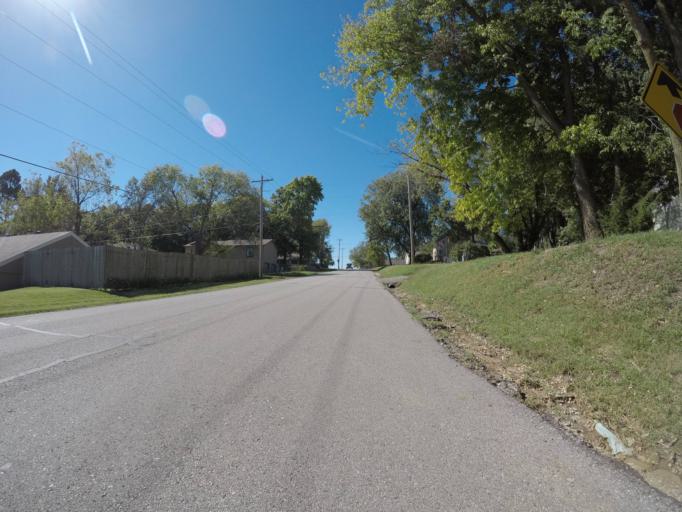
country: US
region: Kansas
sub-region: Douglas County
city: Eudora
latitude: 38.9389
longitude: -95.1058
